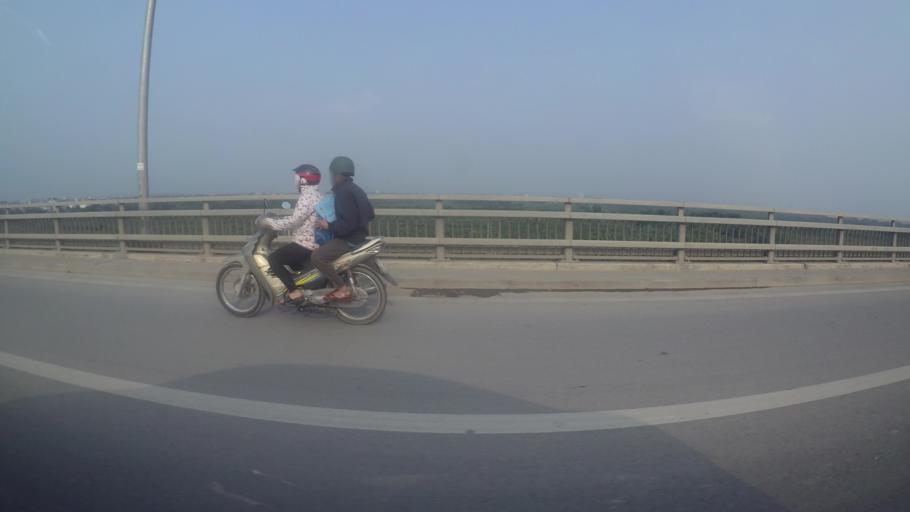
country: VN
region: Ha Noi
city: Tay Ho
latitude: 21.1059
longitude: 105.8261
